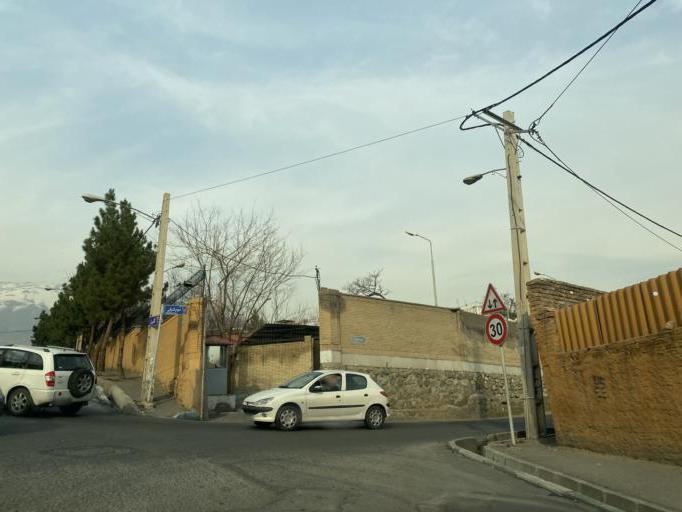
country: IR
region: Tehran
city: Tajrish
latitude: 35.8025
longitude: 51.4840
